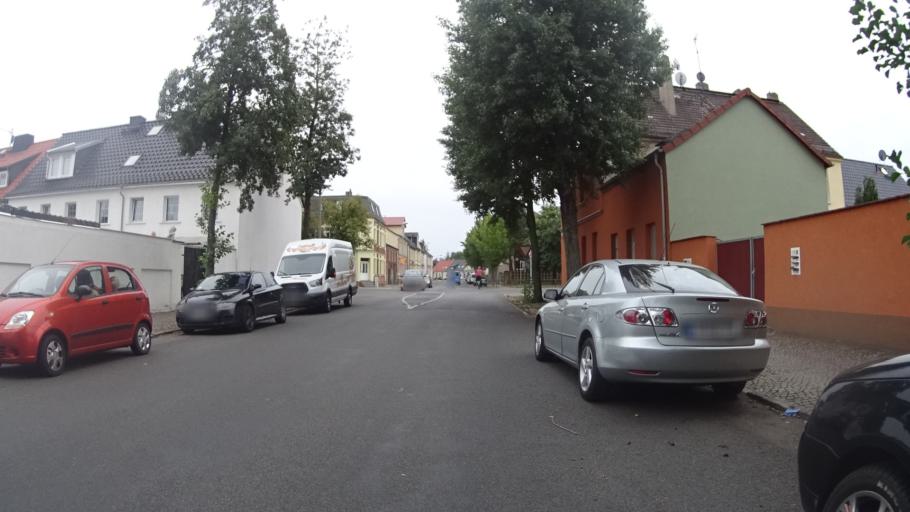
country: DE
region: Brandenburg
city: Luckenwalde
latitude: 52.0850
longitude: 13.1599
